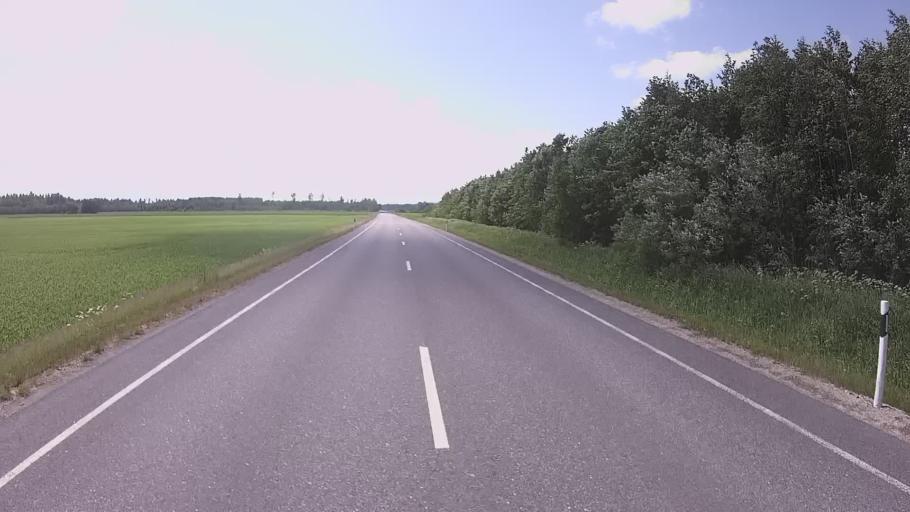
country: EE
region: Tartu
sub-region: Tartu linn
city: Tartu
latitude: 58.3908
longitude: 26.8914
